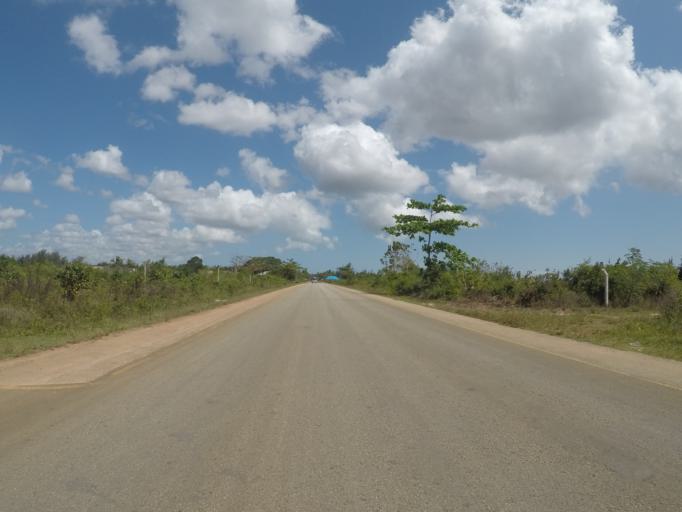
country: TZ
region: Zanzibar Central/South
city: Koani
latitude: -6.1590
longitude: 39.3298
